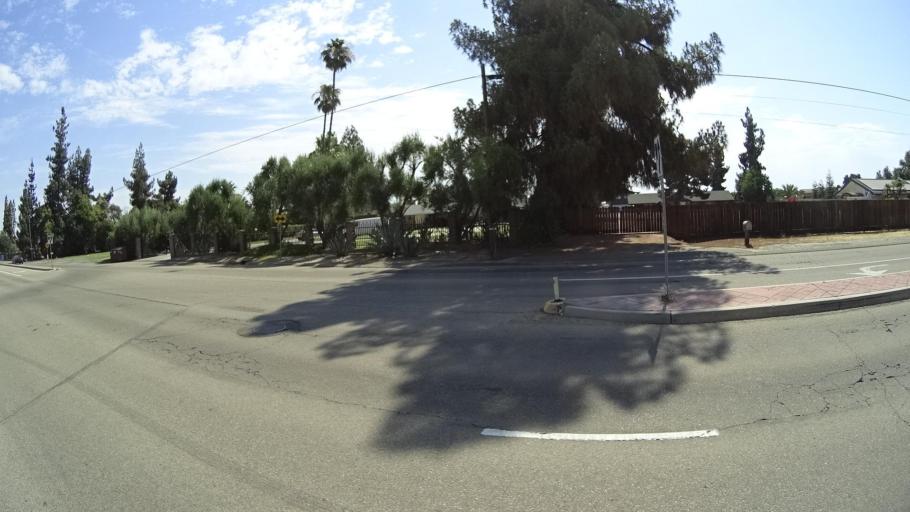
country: US
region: California
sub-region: Fresno County
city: Sunnyside
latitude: 36.7200
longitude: -119.6823
